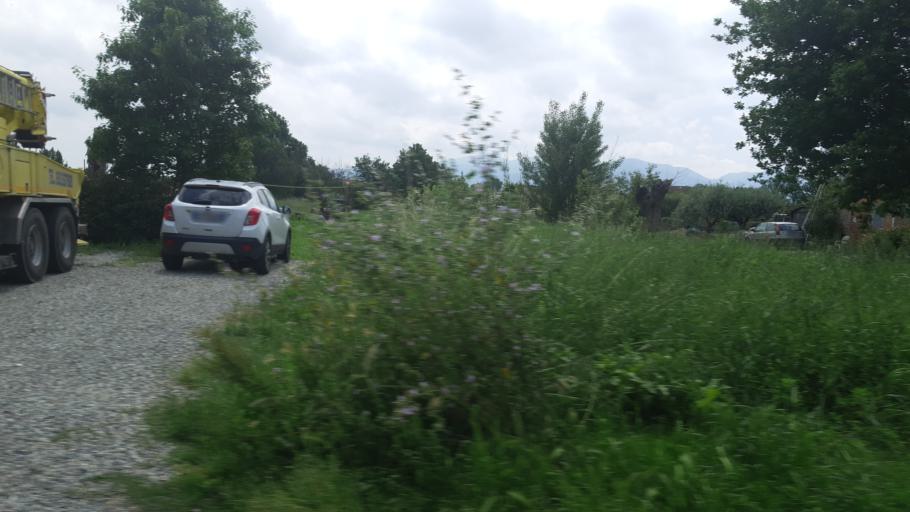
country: IT
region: Tuscany
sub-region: Provincia di Lucca
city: Capannori
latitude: 43.8638
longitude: 10.5568
